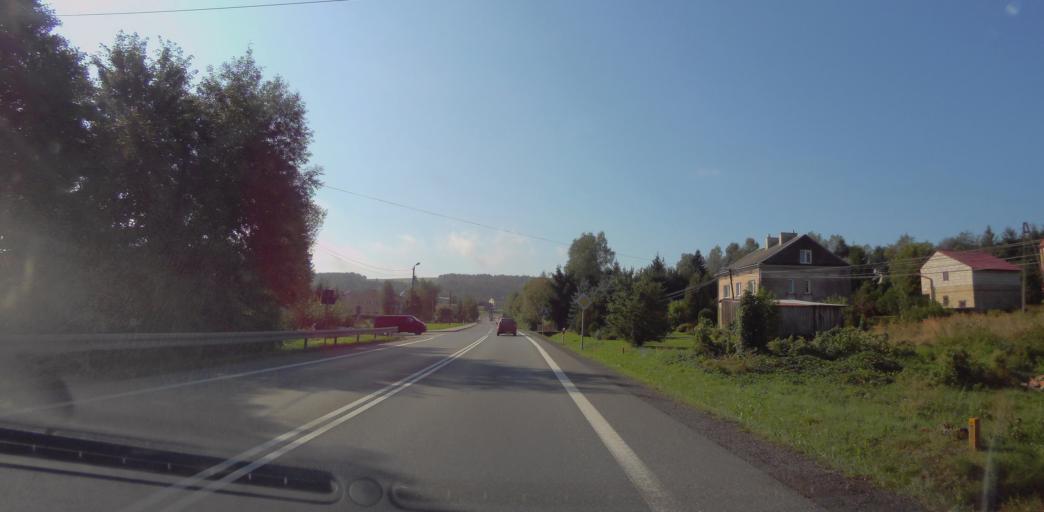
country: PL
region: Subcarpathian Voivodeship
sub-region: Powiat strzyzowski
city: Niebylec
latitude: 49.8608
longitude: 21.9033
